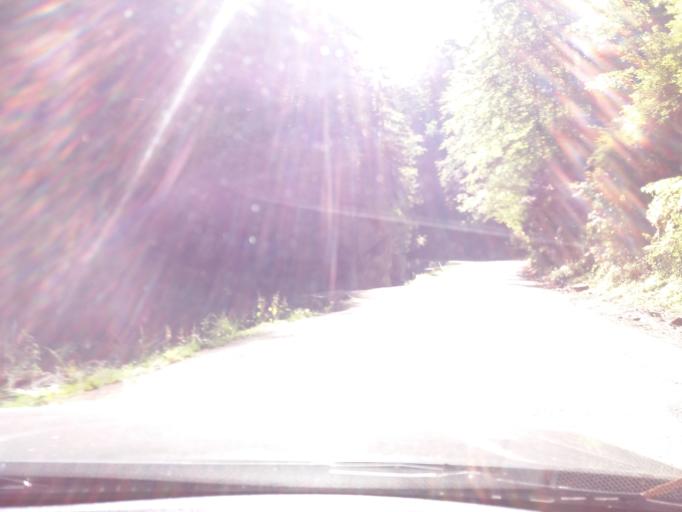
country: RO
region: Hunedoara
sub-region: Oras Petrila
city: Petrila
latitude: 45.4111
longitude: 23.4800
